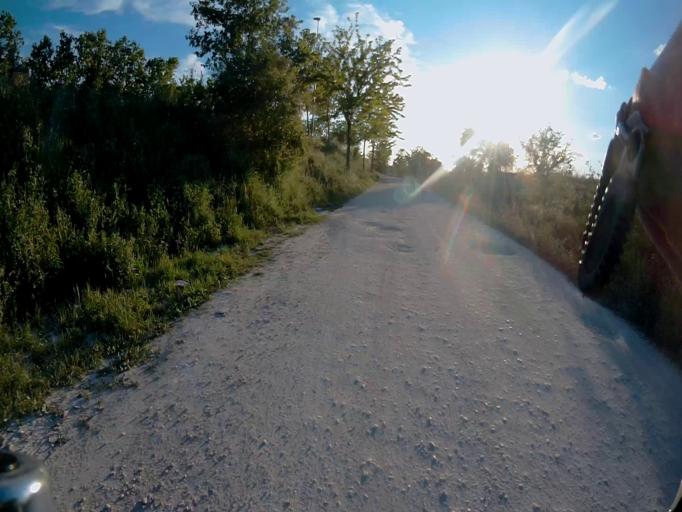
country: ES
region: Madrid
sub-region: Provincia de Madrid
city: Leganes
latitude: 40.3262
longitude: -3.7886
